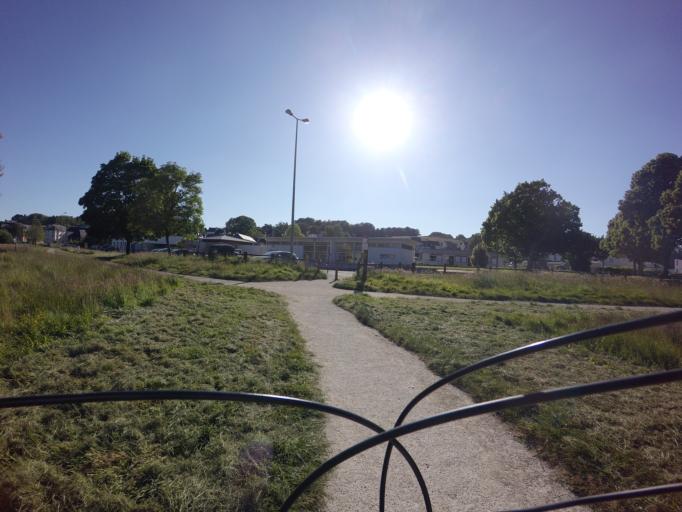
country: FR
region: Brittany
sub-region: Departement du Finistere
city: Quimper
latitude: 48.0068
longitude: -4.1158
